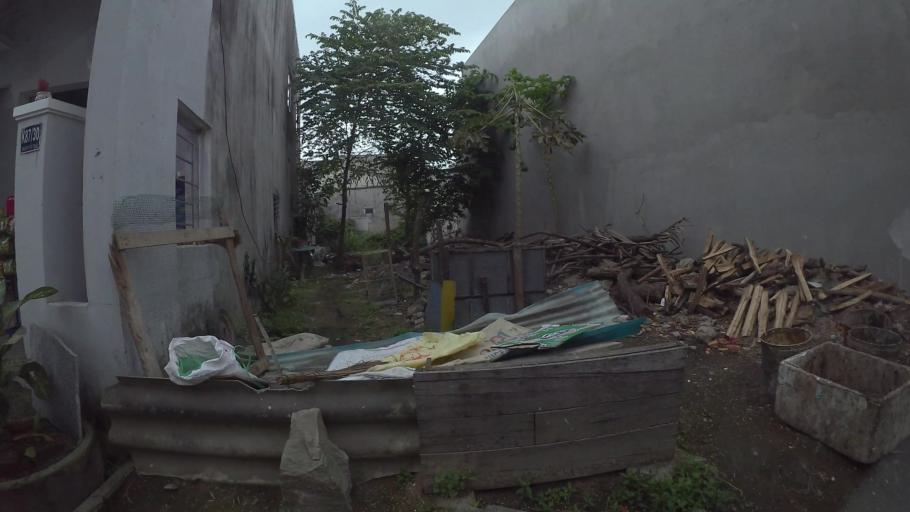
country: VN
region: Da Nang
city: Lien Chieu
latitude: 16.0522
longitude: 108.1576
